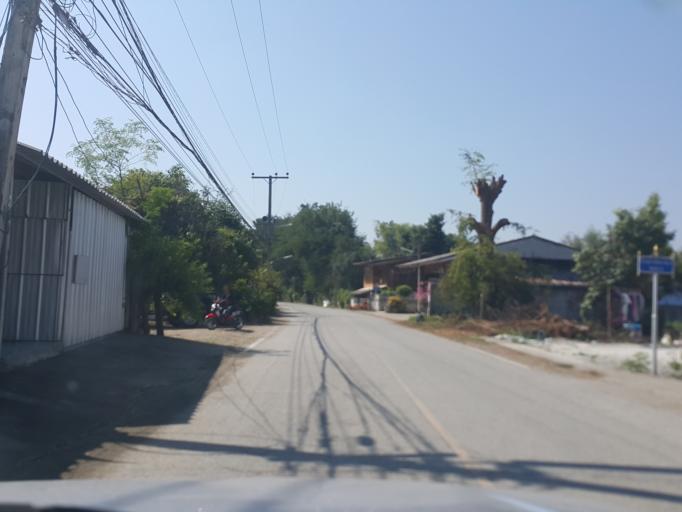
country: TH
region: Chiang Mai
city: San Kamphaeng
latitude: 18.8005
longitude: 99.1434
